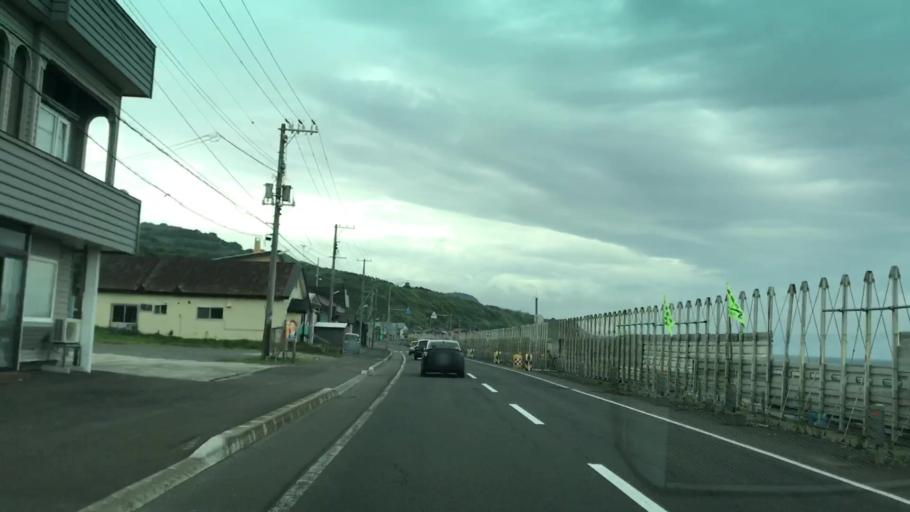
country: JP
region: Hokkaido
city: Iwanai
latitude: 42.8601
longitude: 140.3491
